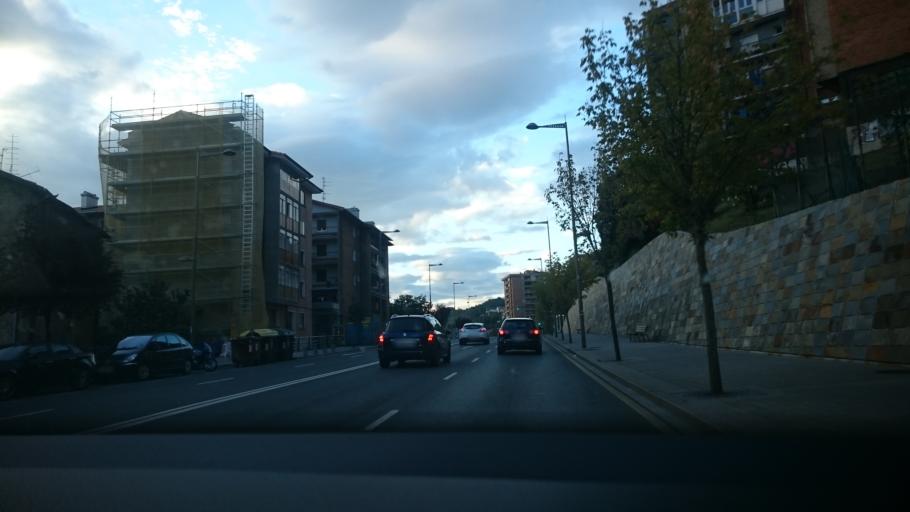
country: ES
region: Basque Country
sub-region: Bizkaia
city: Bilbao
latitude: 43.2683
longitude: -2.9193
